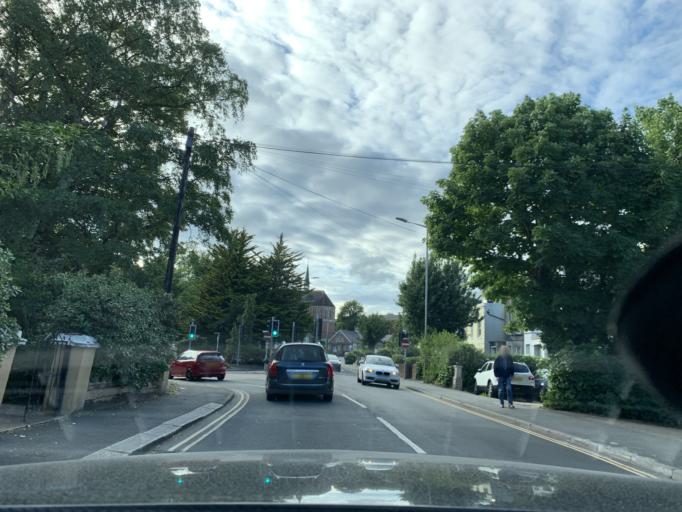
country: GB
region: England
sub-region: East Sussex
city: Saint Leonards-on-Sea
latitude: 50.8644
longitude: 0.5576
